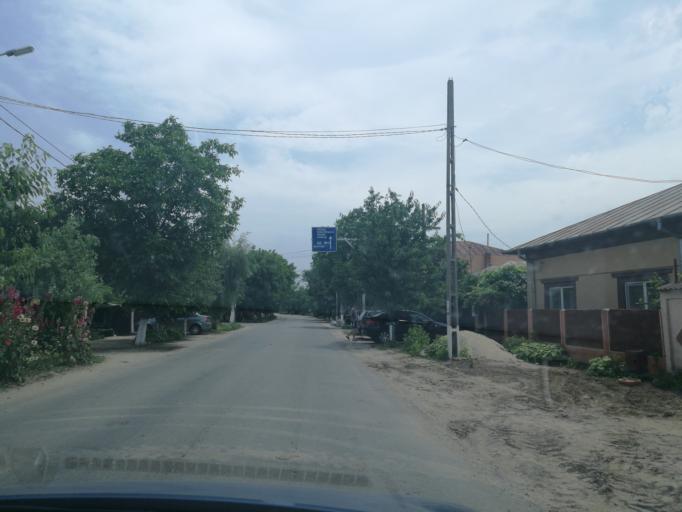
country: RO
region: Ilfov
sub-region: Comuna Vidra
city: Vidra
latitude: 44.2622
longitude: 26.1637
